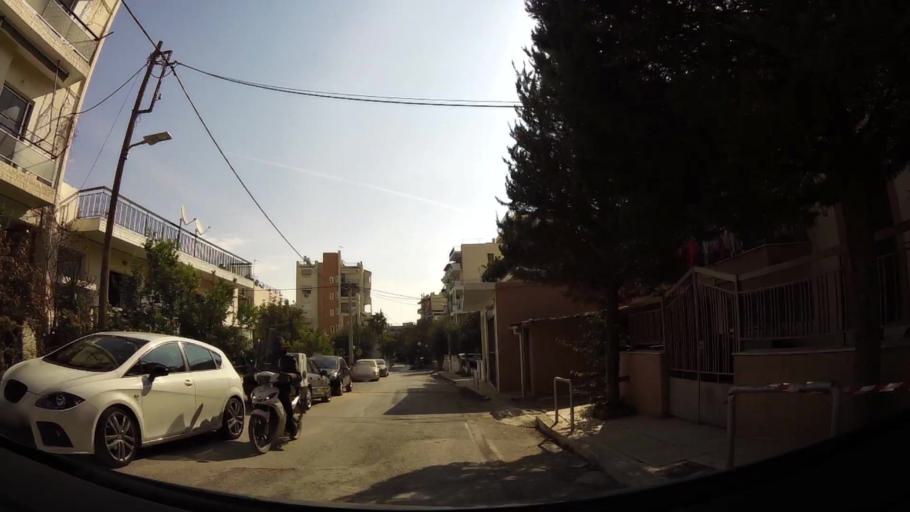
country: GR
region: Attica
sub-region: Nomarchia Athinas
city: Kamateron
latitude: 38.0602
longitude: 23.7118
